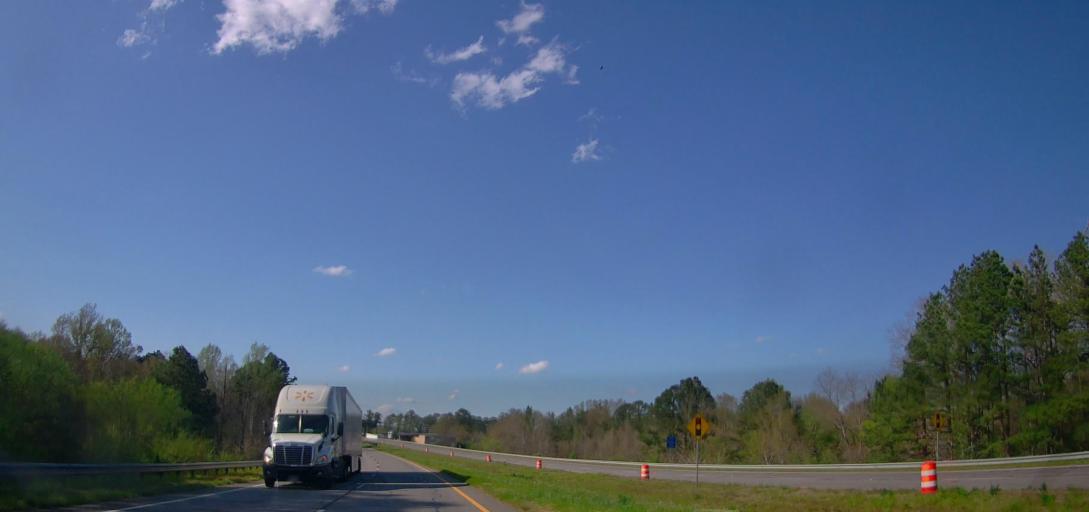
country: US
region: Georgia
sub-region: Baldwin County
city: Milledgeville
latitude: 33.0695
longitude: -83.2492
